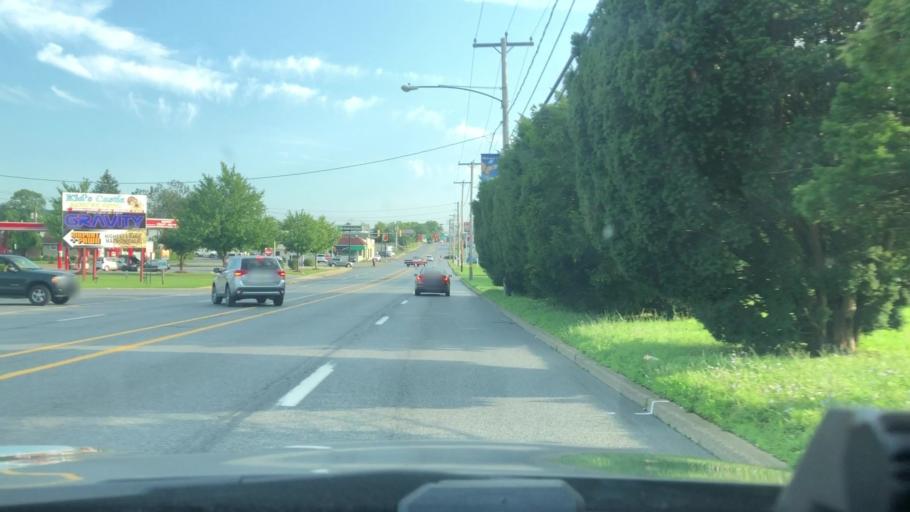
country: US
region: Pennsylvania
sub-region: Lehigh County
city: Fullerton
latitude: 40.6289
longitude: -75.4421
